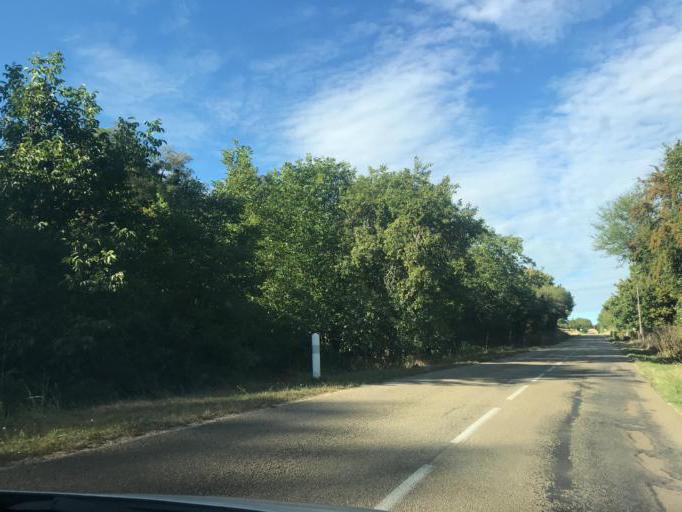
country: FR
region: Bourgogne
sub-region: Departement de l'Yonne
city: Fontenailles
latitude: 47.5503
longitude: 3.4260
